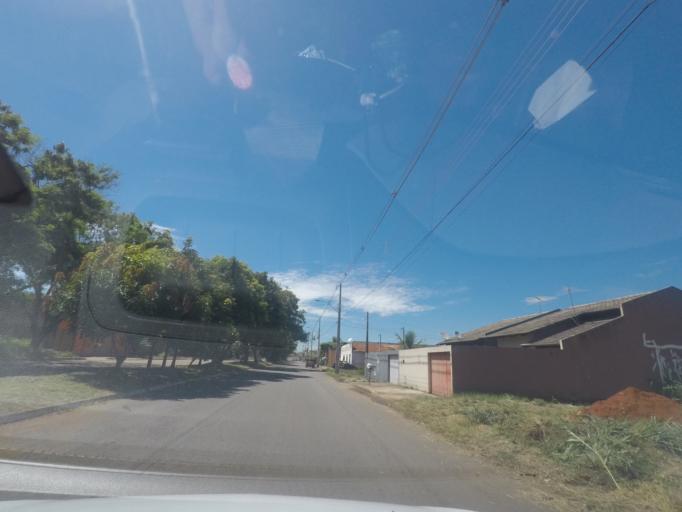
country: BR
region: Goias
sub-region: Aparecida De Goiania
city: Aparecida de Goiania
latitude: -16.7812
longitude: -49.3365
